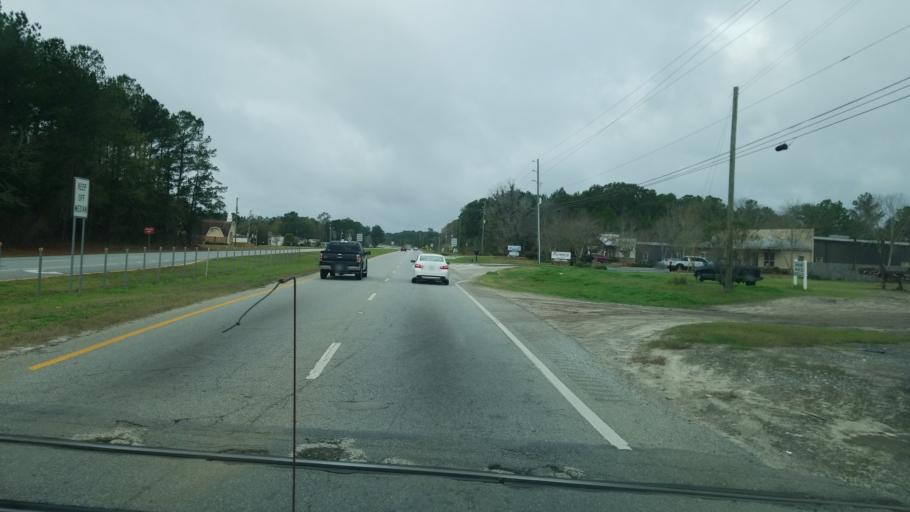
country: US
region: Georgia
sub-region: Lowndes County
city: Valdosta
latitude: 30.8818
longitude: -83.2503
